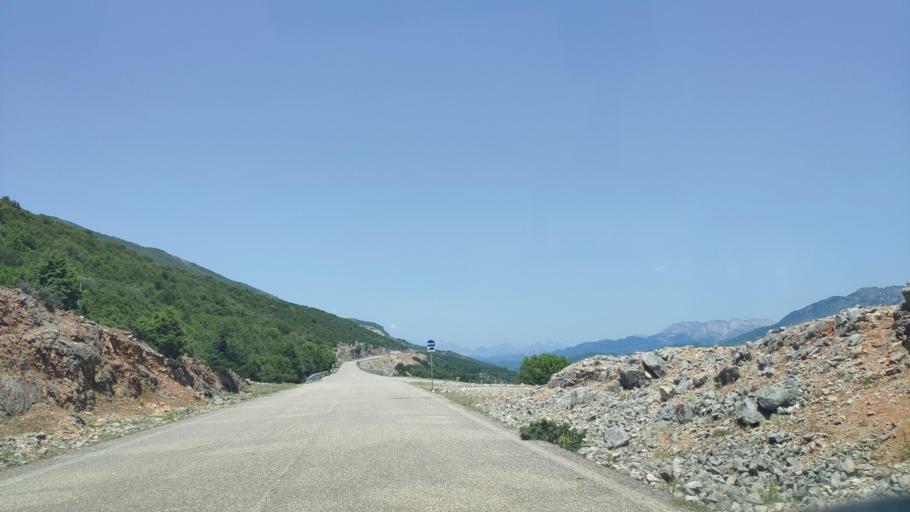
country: GR
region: Thessaly
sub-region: Nomos Kardhitsas
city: Anthiro
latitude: 39.1166
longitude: 21.4060
